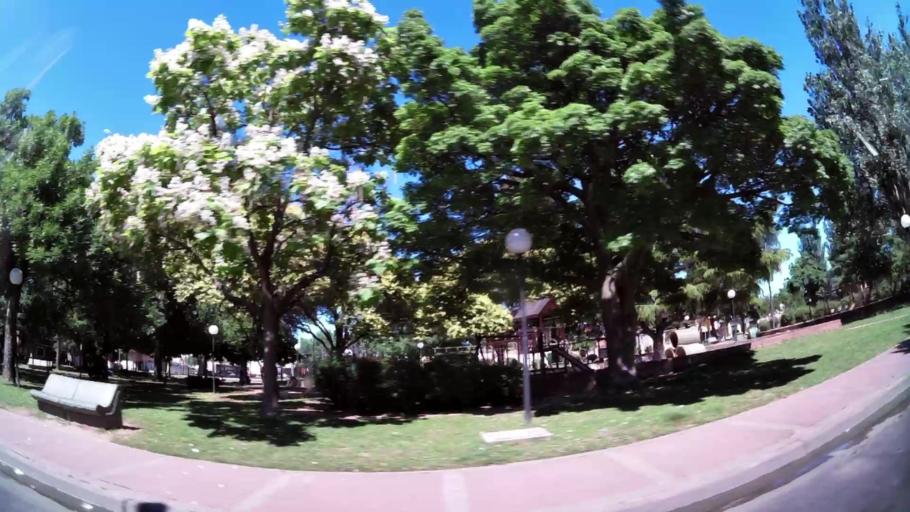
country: AR
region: Buenos Aires
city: Hurlingham
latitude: -34.5012
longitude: -58.6262
